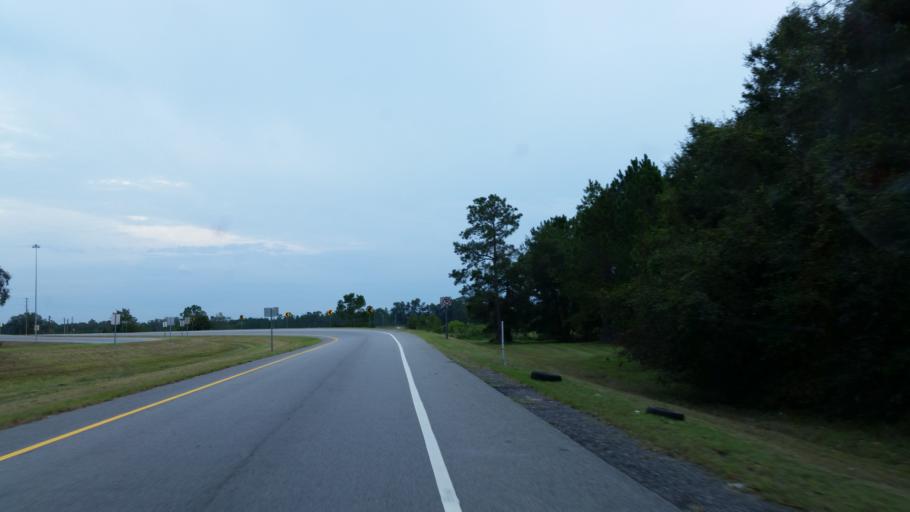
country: US
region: Georgia
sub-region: Lowndes County
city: Valdosta
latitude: 30.7788
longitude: -83.2984
